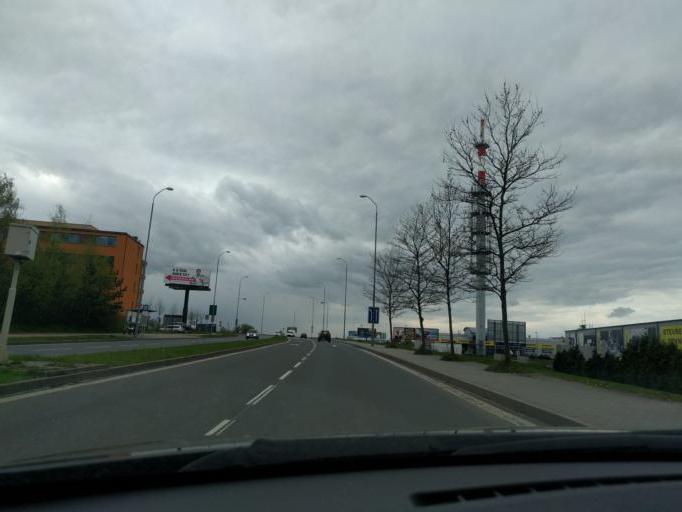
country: CZ
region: Plzensky
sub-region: Okres Plzen-Mesto
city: Pilsen
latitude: 49.7748
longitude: 13.3544
